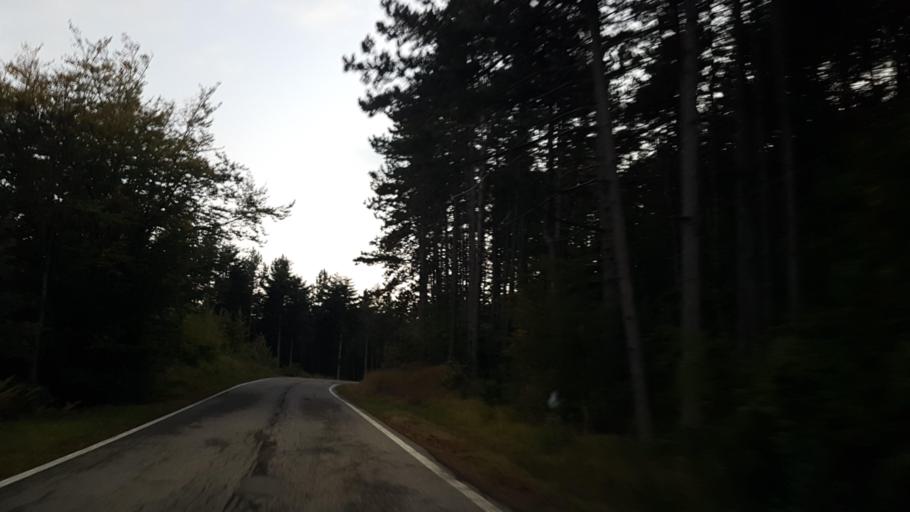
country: IT
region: Emilia-Romagna
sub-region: Provincia di Parma
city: Tornolo
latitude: 44.4353
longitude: 9.6291
